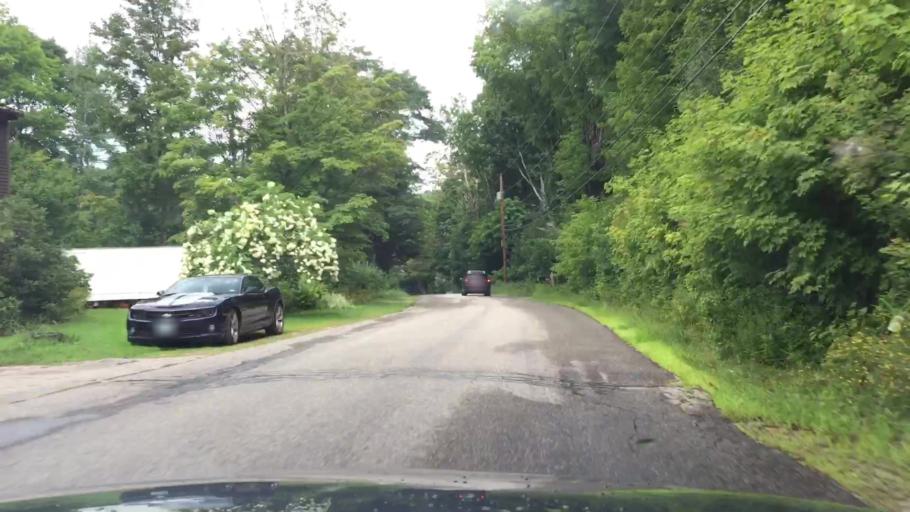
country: US
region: New Hampshire
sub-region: Grafton County
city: Holderness
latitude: 43.7283
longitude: -71.5765
